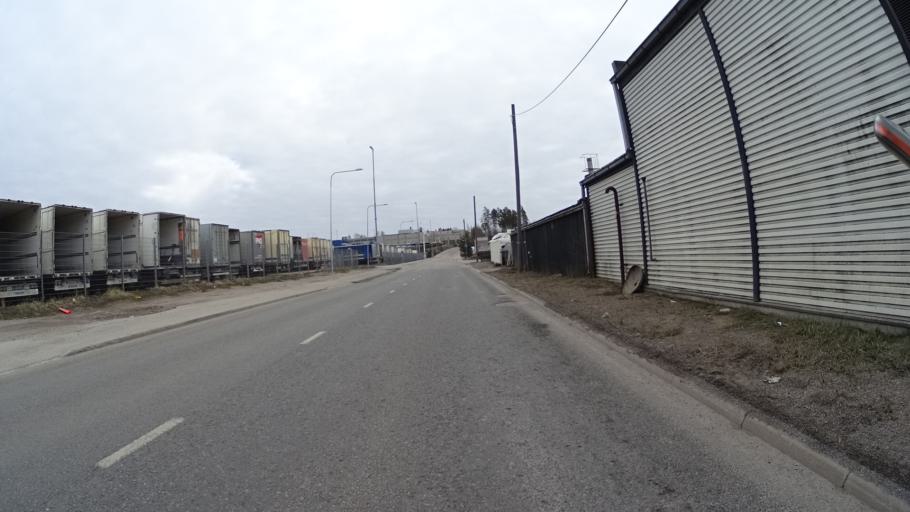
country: FI
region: Uusimaa
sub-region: Helsinki
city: Teekkarikylae
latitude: 60.2995
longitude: 24.9051
